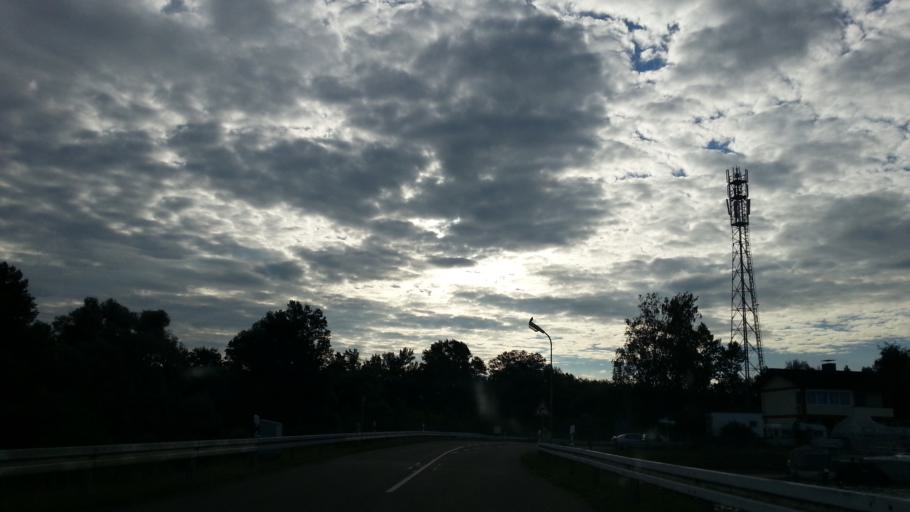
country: DE
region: Baden-Wuerttemberg
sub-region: Freiburg Region
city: Schwanau
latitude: 48.3668
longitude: 7.7357
